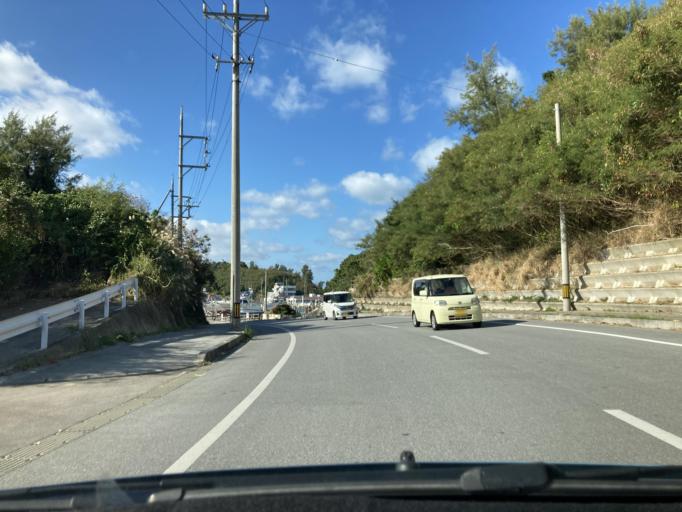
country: JP
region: Okinawa
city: Katsuren-haebaru
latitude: 26.3183
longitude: 127.9178
